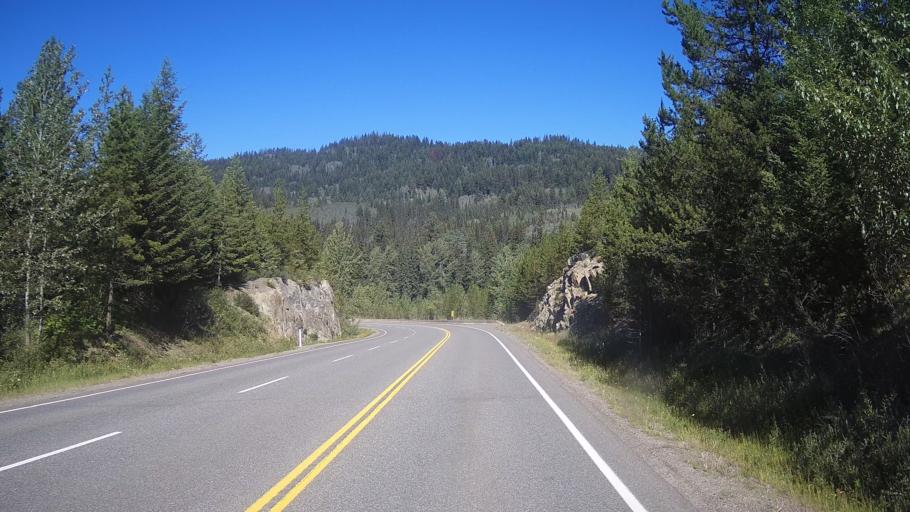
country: CA
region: British Columbia
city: Kamloops
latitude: 51.4769
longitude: -120.4822
